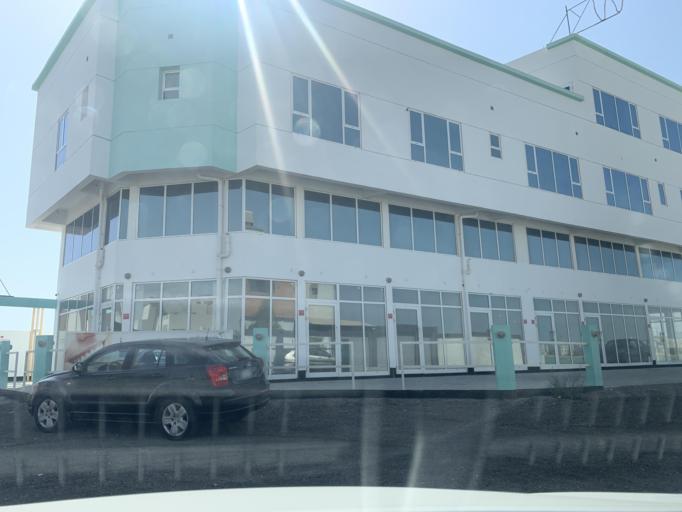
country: BH
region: Manama
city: Jidd Hafs
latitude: 26.2312
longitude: 50.4671
